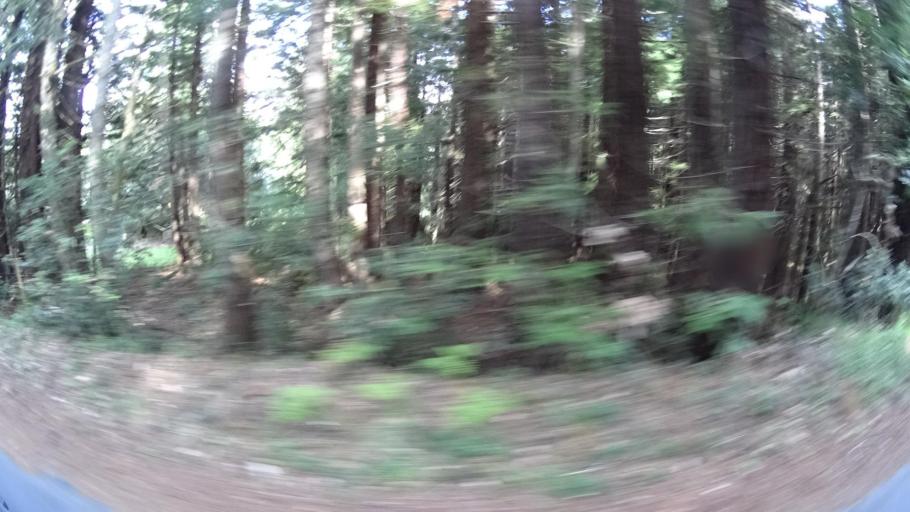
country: US
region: California
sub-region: Humboldt County
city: Bayside
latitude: 40.7646
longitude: -124.0000
